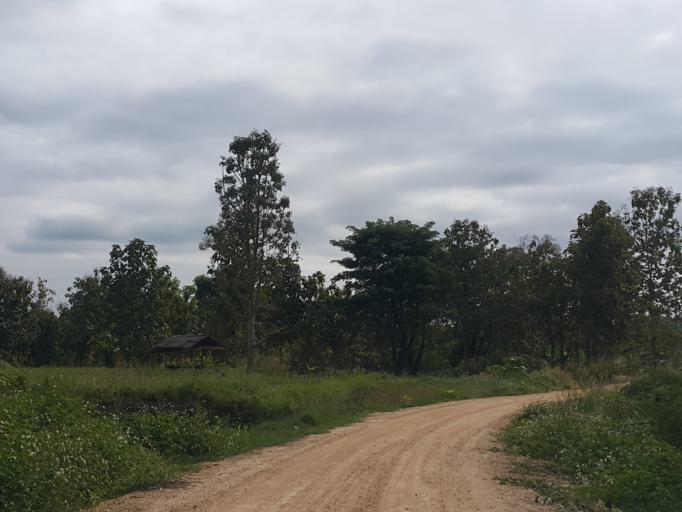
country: TH
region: Lampang
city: Hang Chat
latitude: 18.4865
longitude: 99.4013
